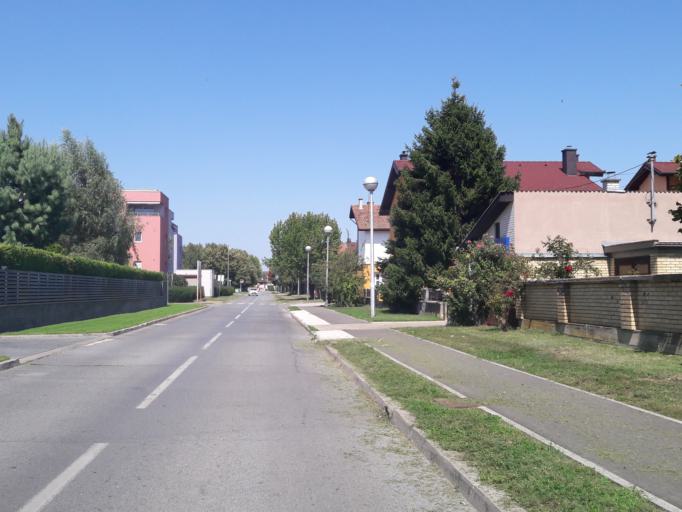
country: HR
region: Osjecko-Baranjska
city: Visnjevac
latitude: 45.5599
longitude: 18.6422
